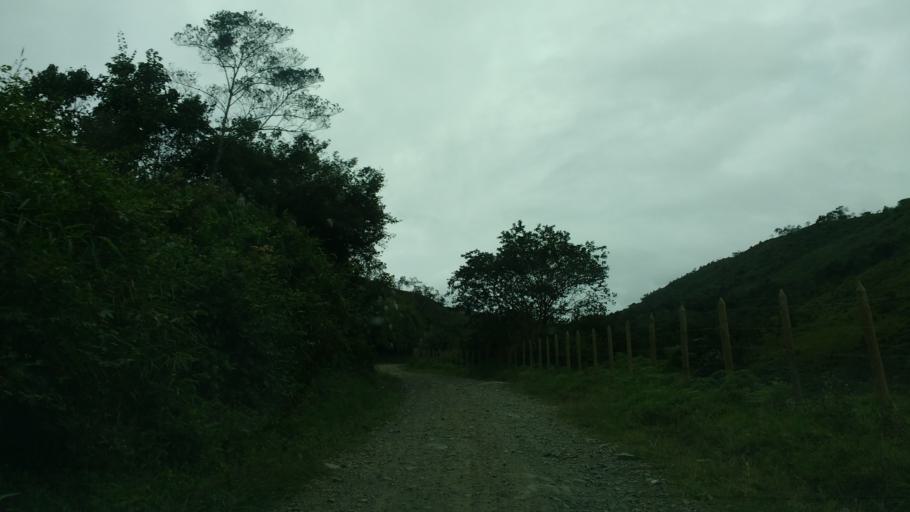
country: CO
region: Antioquia
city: Concepcion
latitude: 6.3809
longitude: -75.2266
